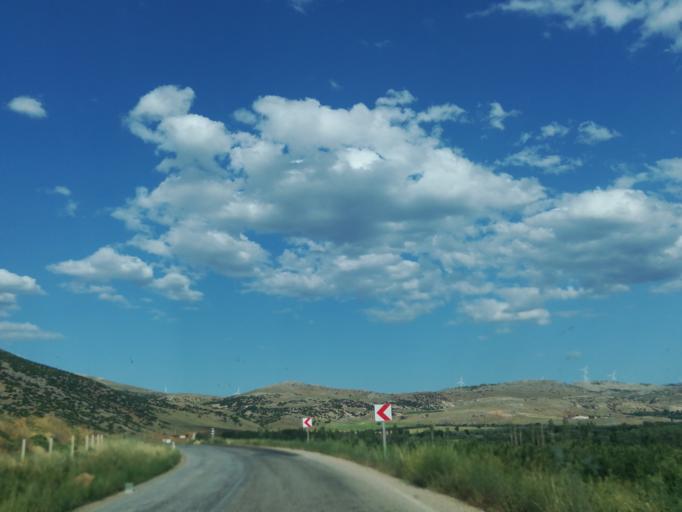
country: TR
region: Afyonkarahisar
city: Dinar
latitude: 38.0987
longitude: 30.1439
